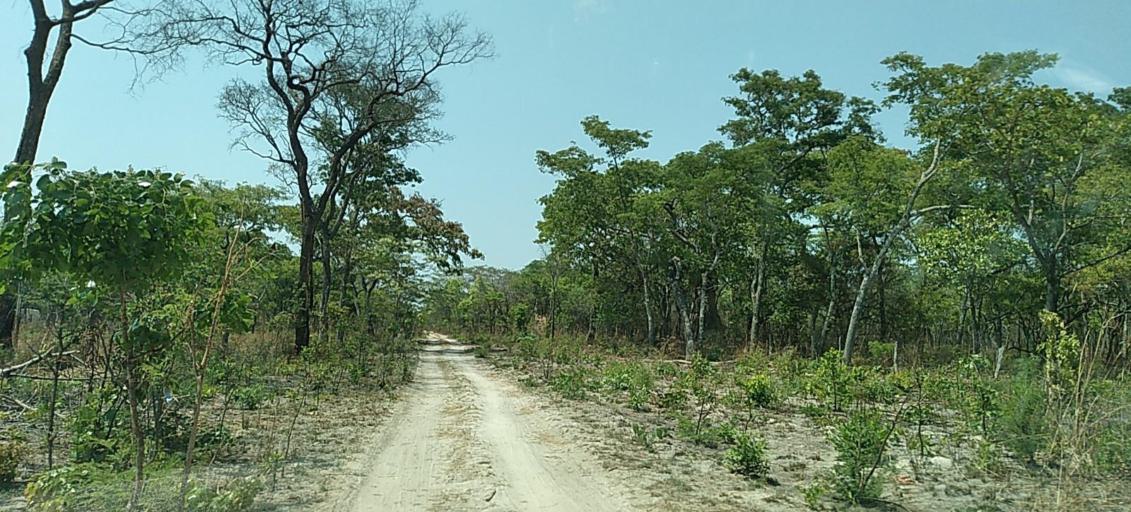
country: ZM
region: Copperbelt
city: Mpongwe
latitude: -13.8329
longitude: 28.0596
